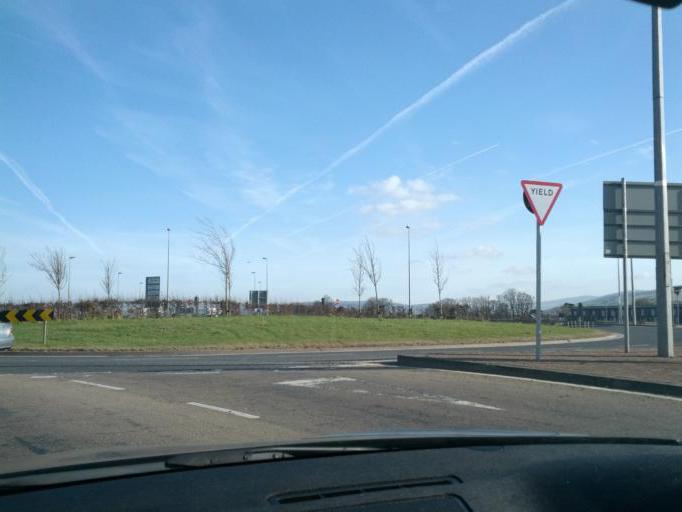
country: IE
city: Jobstown
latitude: 53.3038
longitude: -6.4208
